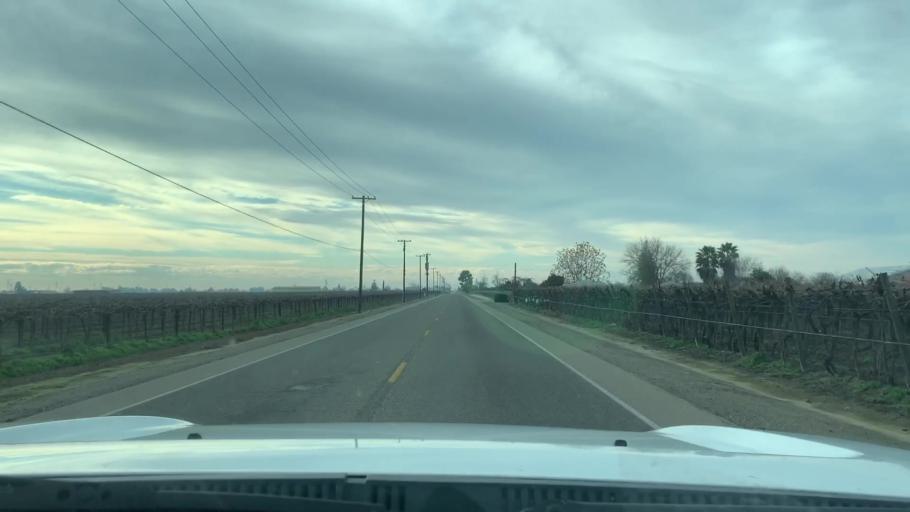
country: US
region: California
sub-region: Fresno County
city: Fowler
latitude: 36.6055
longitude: -119.7239
